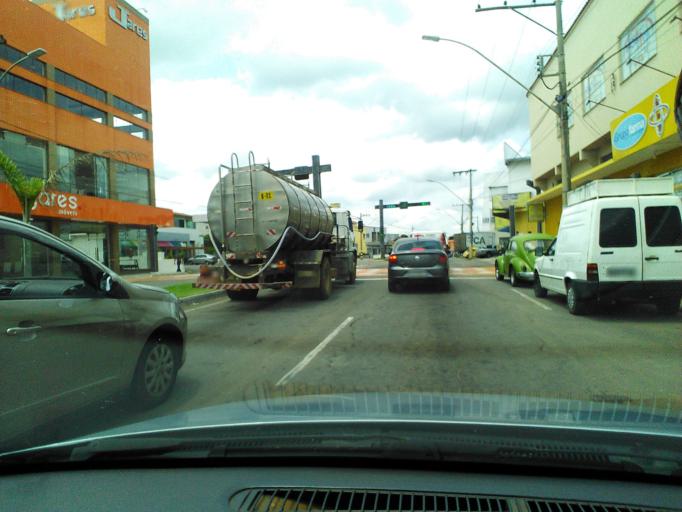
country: BR
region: Minas Gerais
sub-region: Tres Coracoes
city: Tres Coracoes
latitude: -21.6866
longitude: -45.2615
